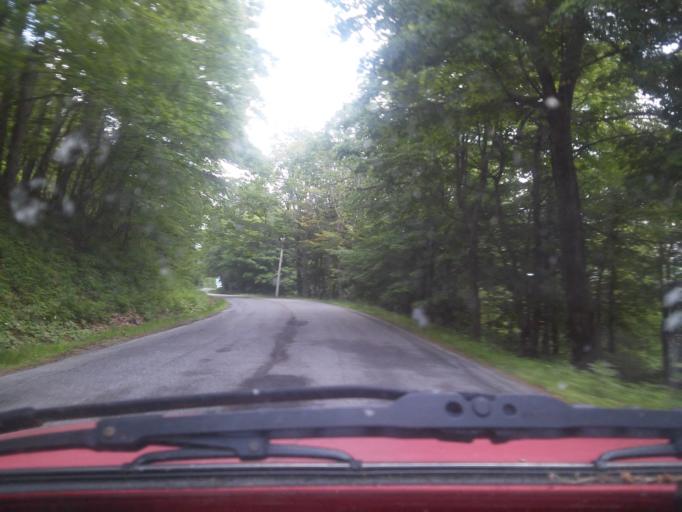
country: US
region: Virginia
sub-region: Giles County
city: Pembroke
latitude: 37.3539
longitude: -80.5399
